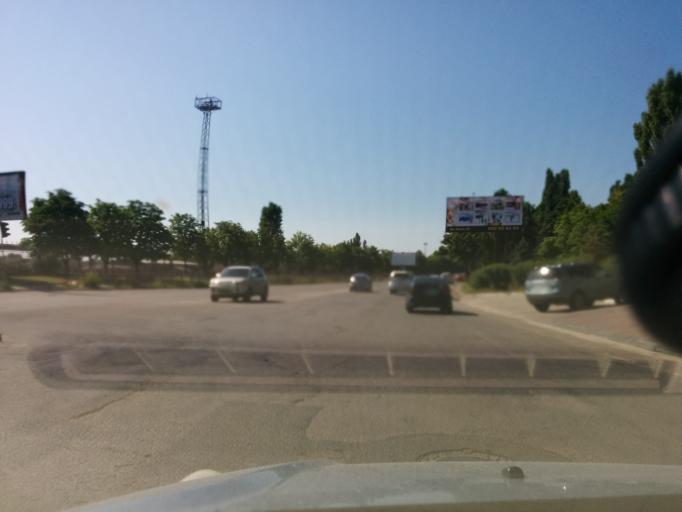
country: MD
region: Chisinau
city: Chisinau
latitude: 47.0209
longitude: 28.8558
